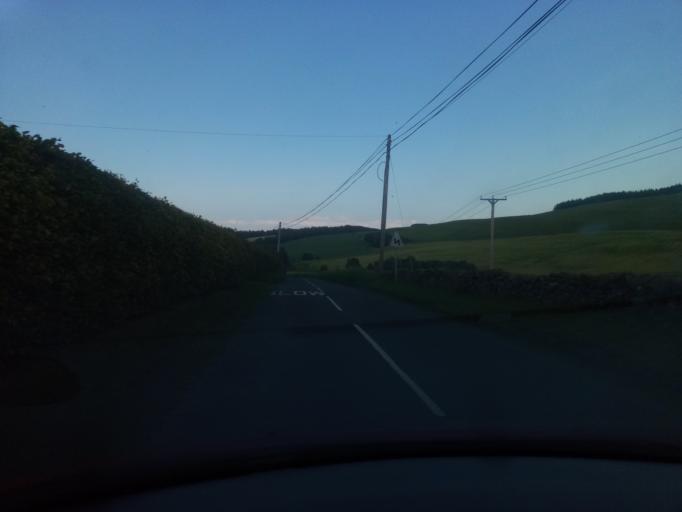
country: GB
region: Scotland
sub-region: The Scottish Borders
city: Selkirk
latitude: 55.5116
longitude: -2.9372
